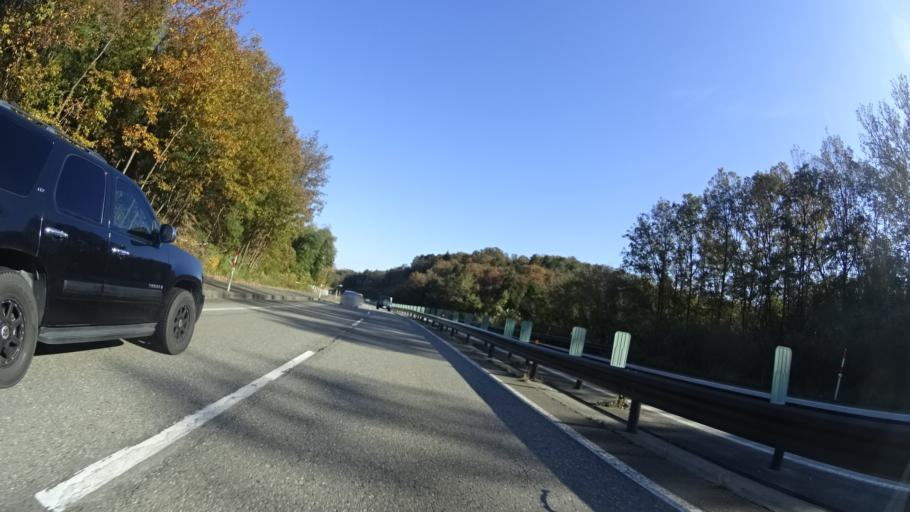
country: JP
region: Ishikawa
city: Komatsu
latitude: 36.3633
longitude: 136.4594
